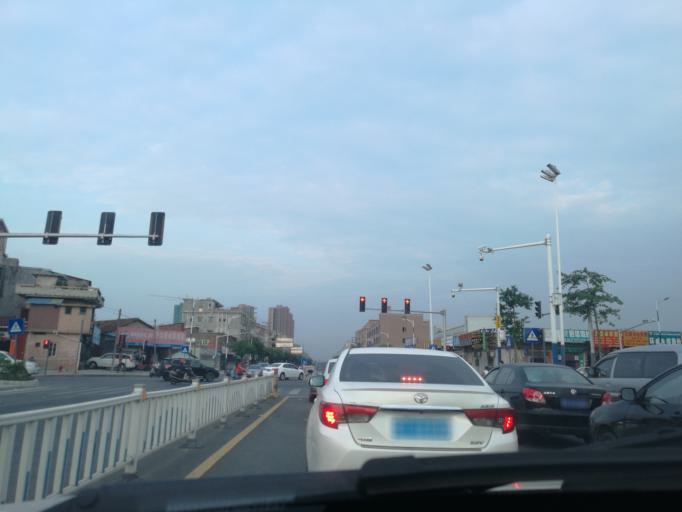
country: CN
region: Guangdong
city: Hengli
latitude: 23.0394
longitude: 113.9633
